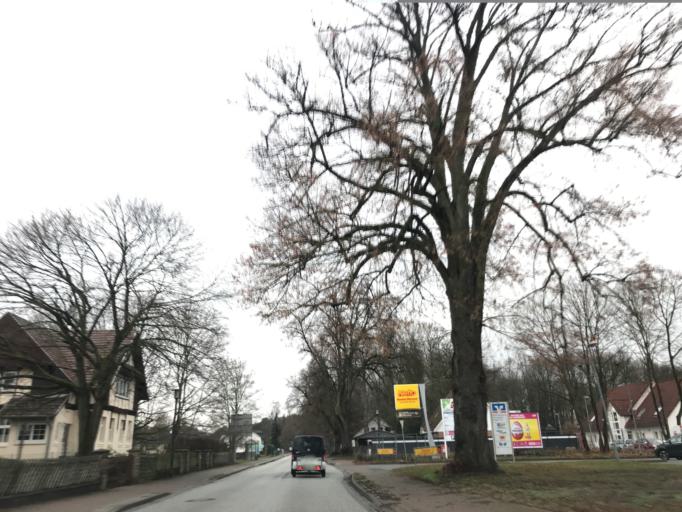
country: DE
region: Brandenburg
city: Lindow
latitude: 52.9752
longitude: 12.9867
